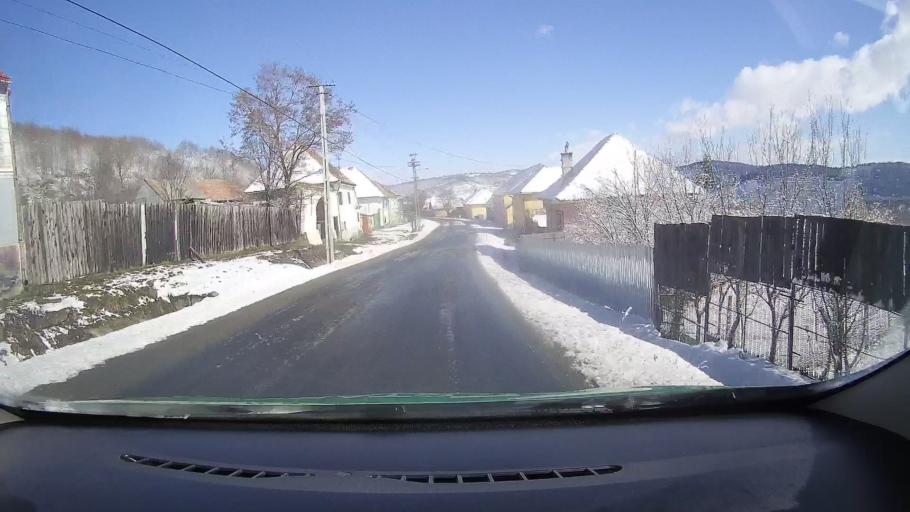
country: RO
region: Sibiu
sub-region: Comuna Rosia
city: Rosia
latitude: 45.7944
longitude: 24.3819
